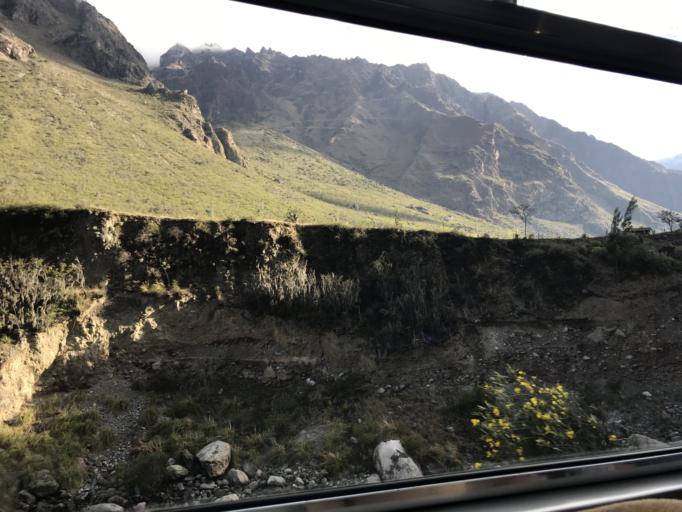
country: PE
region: Cusco
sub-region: Provincia de Urubamba
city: Ollantaytambo
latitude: -13.2212
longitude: -72.3930
